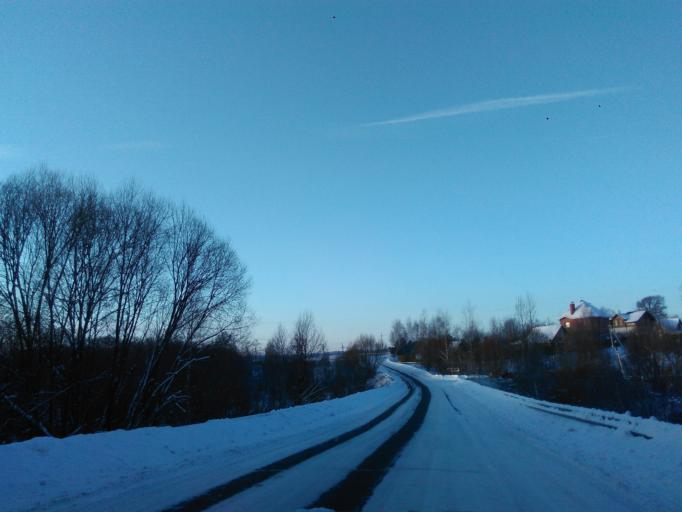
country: RU
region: Tverskaya
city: Zavidovo
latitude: 56.6090
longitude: 36.6146
